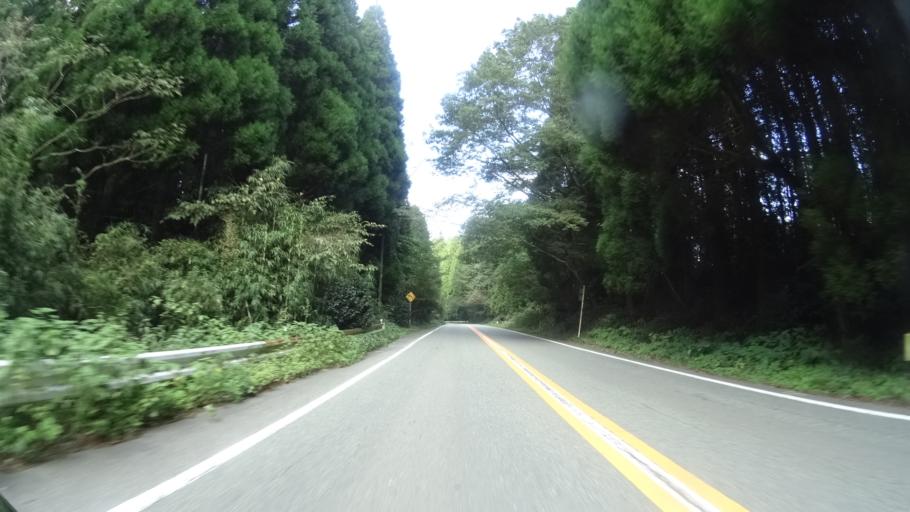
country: JP
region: Kumamoto
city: Aso
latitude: 33.0723
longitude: 131.0635
